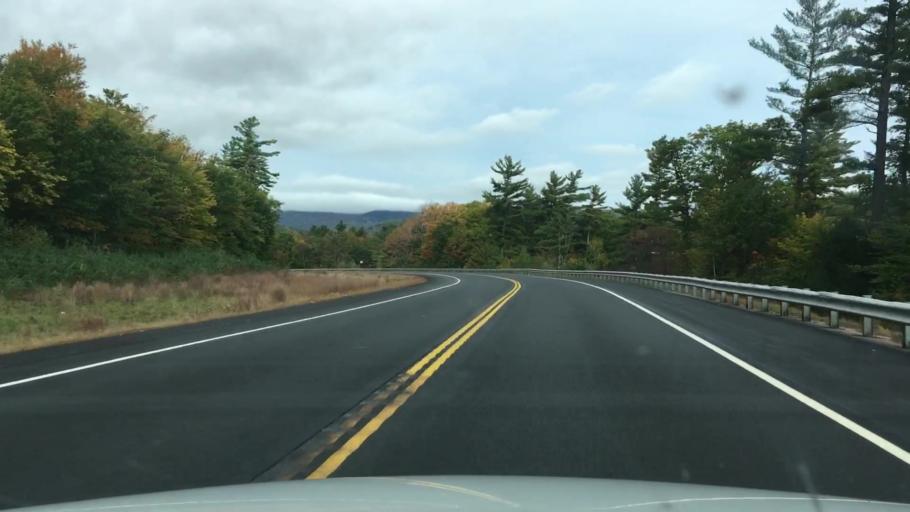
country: US
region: New Hampshire
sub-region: Coos County
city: Gorham
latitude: 44.3950
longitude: -70.9904
